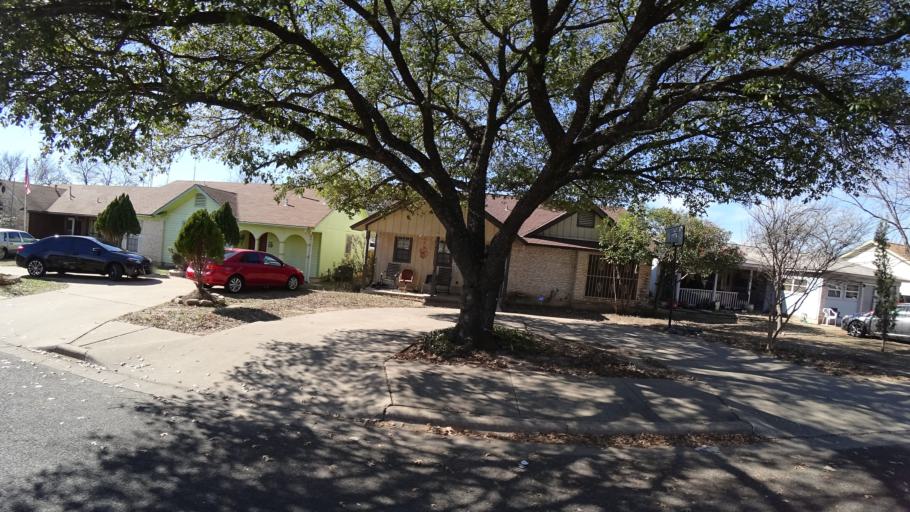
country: US
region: Texas
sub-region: Travis County
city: Wells Branch
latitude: 30.3691
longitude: -97.6894
